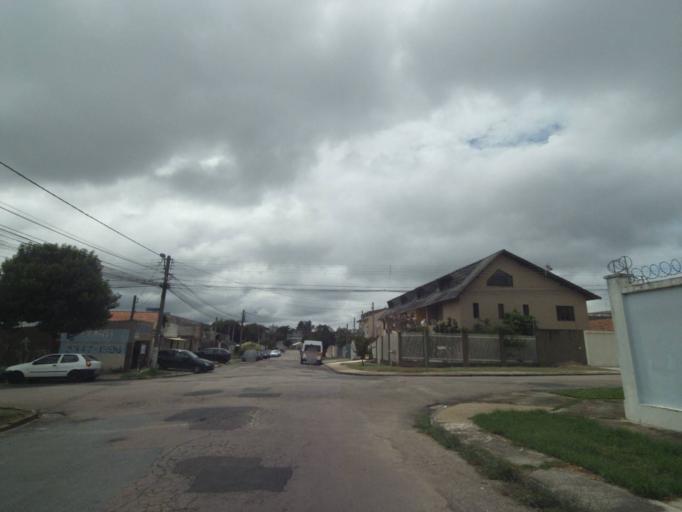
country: BR
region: Parana
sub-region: Curitiba
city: Curitiba
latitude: -25.4883
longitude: -49.3095
